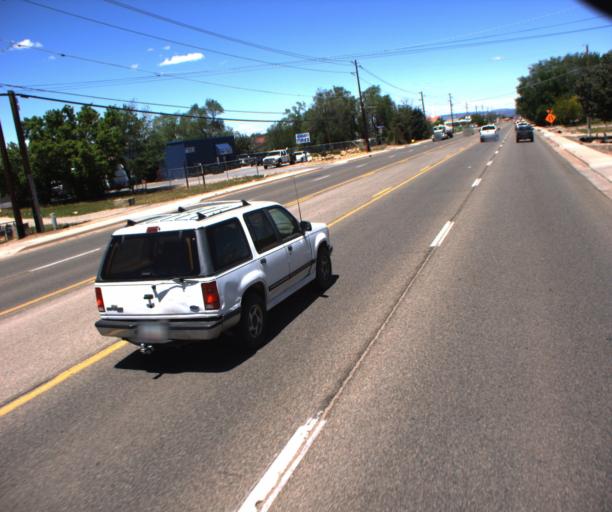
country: US
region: Arizona
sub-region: Yavapai County
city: Chino Valley
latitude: 34.7644
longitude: -112.4534
